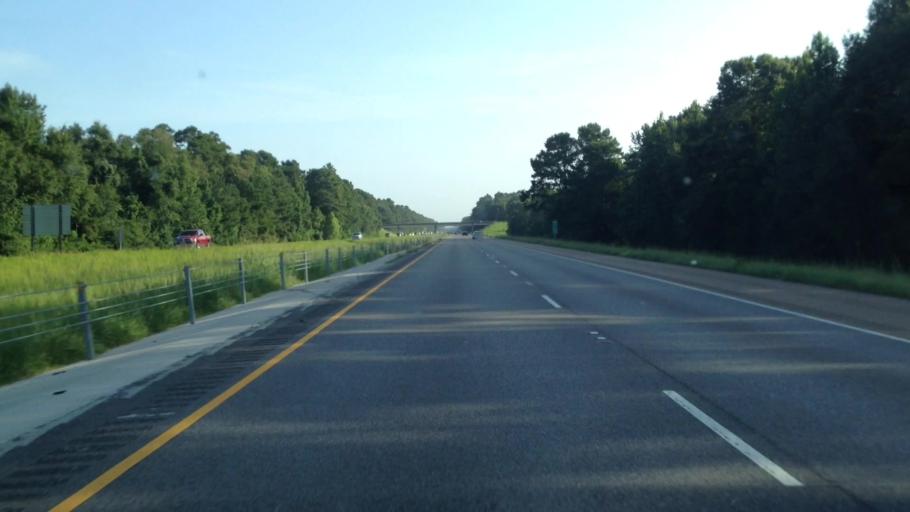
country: US
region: Louisiana
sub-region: Tangipahoa Parish
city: Natalbany
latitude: 30.5395
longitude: -90.5039
